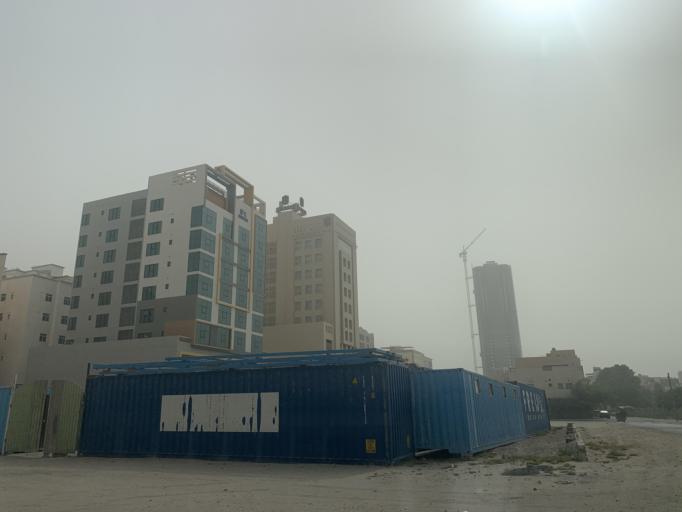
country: BH
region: Manama
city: Jidd Hafs
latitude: 26.2241
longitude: 50.5550
